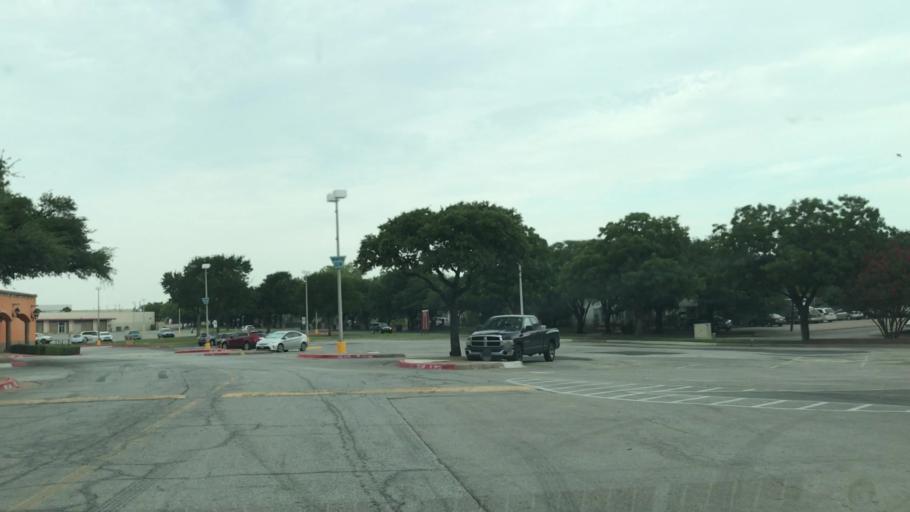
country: US
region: Texas
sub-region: Tarrant County
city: Edgecliff Village
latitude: 32.6881
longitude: -97.3243
